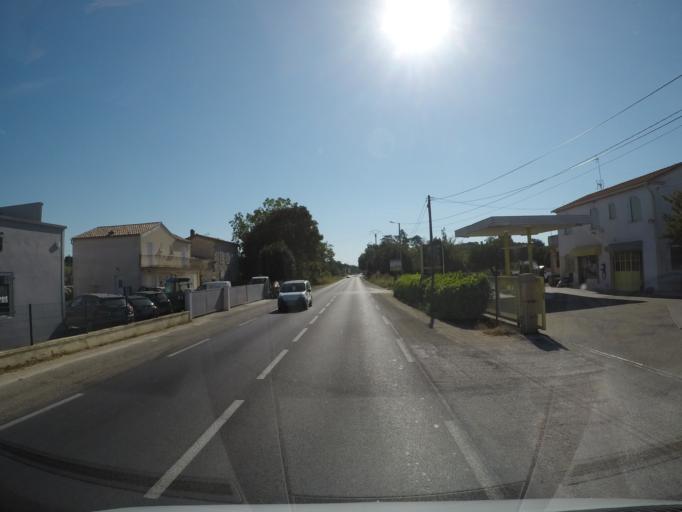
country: FR
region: Languedoc-Roussillon
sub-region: Departement du Gard
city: Moussac
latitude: 43.9765
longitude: 4.2112
